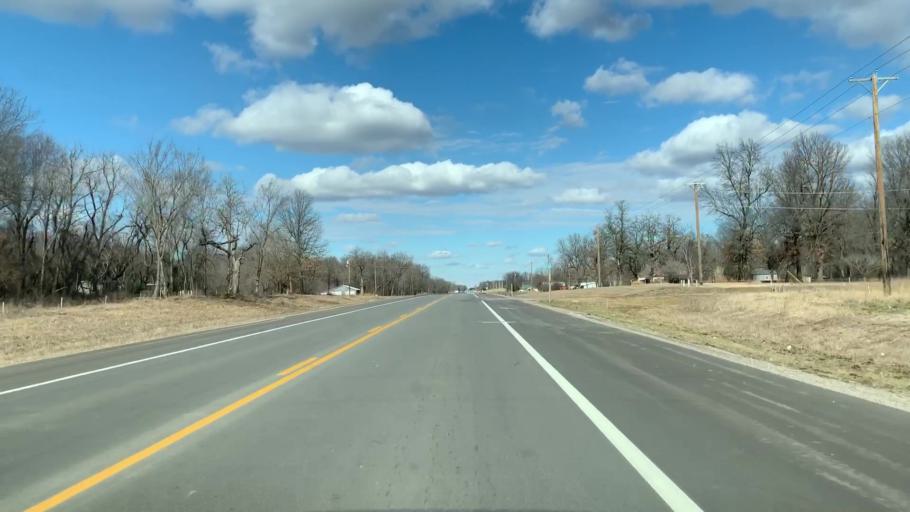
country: US
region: Kansas
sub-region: Cherokee County
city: Columbus
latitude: 37.2298
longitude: -94.8319
